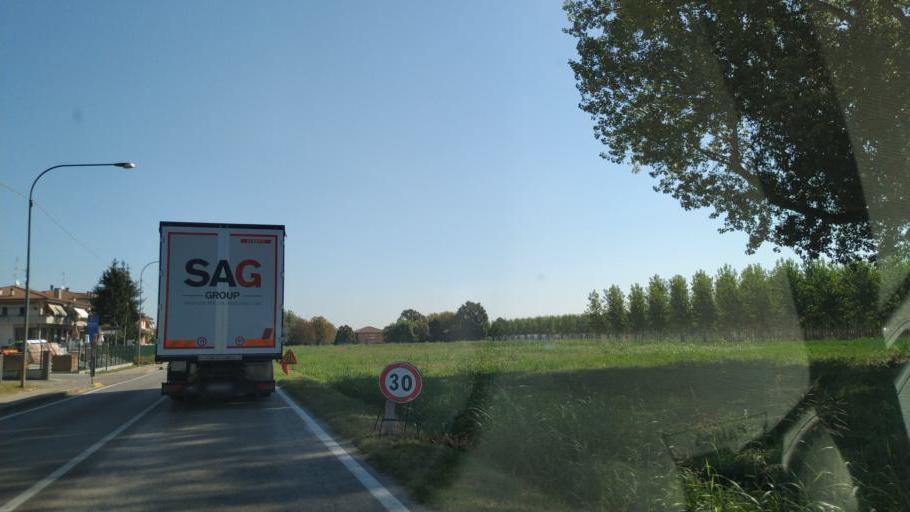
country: IT
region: Emilia-Romagna
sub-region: Provincia di Ferrara
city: Mirabello
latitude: 44.8180
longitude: 11.4495
